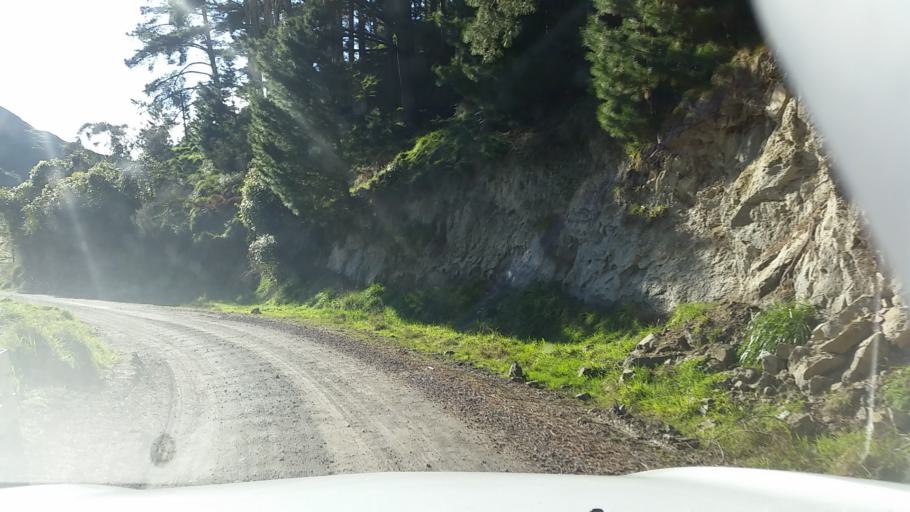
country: NZ
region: Taranaki
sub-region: South Taranaki District
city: Eltham
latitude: -39.5067
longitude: 174.3981
